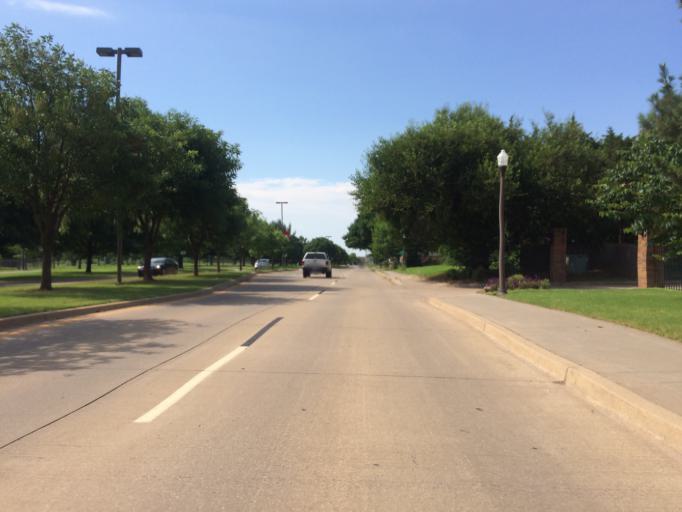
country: US
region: Oklahoma
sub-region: Cleveland County
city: Norman
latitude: 35.1862
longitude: -97.4502
